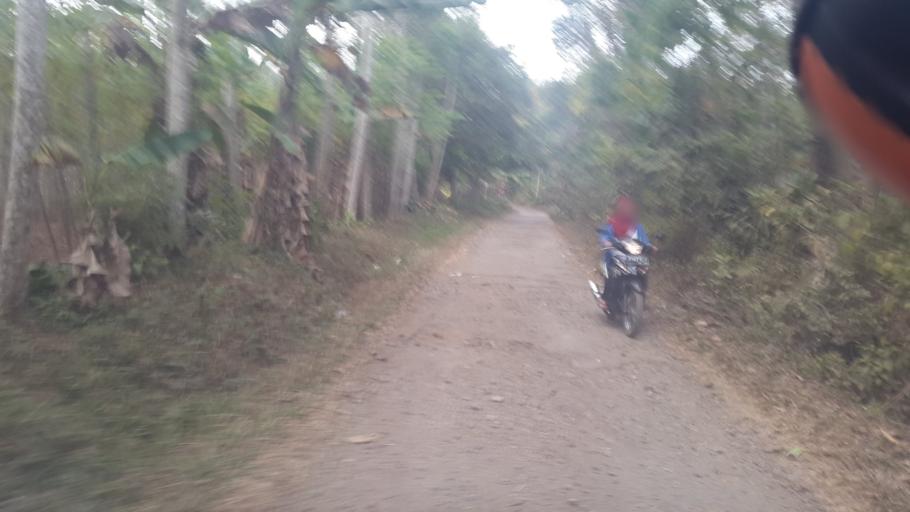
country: ID
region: West Java
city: Ciroyom
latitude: -7.0924
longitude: 106.8590
